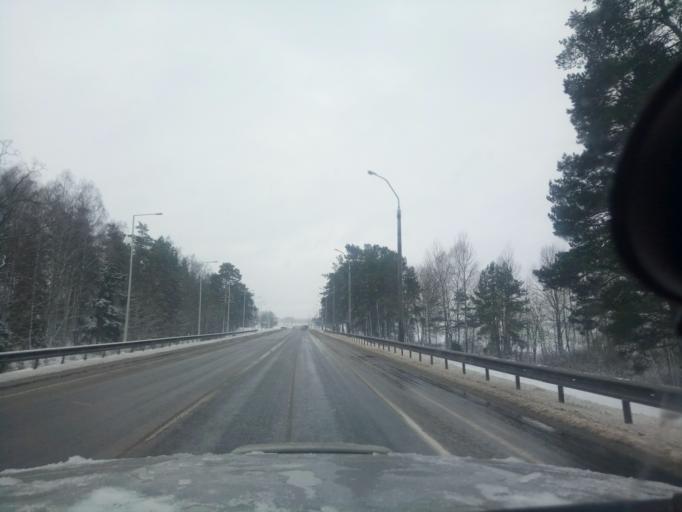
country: BY
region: Minsk
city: Nyasvizh
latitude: 53.2439
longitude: 26.6280
